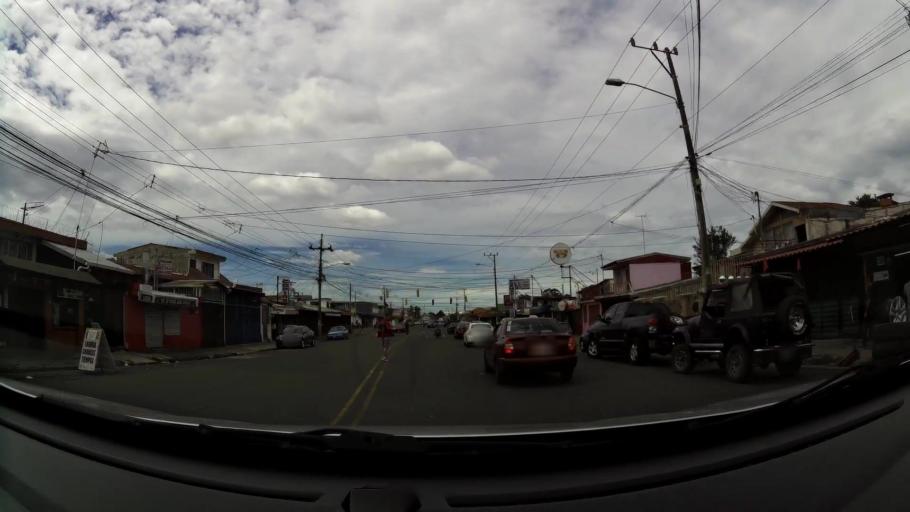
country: CR
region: San Jose
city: San Miguel
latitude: 9.8943
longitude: -84.0562
